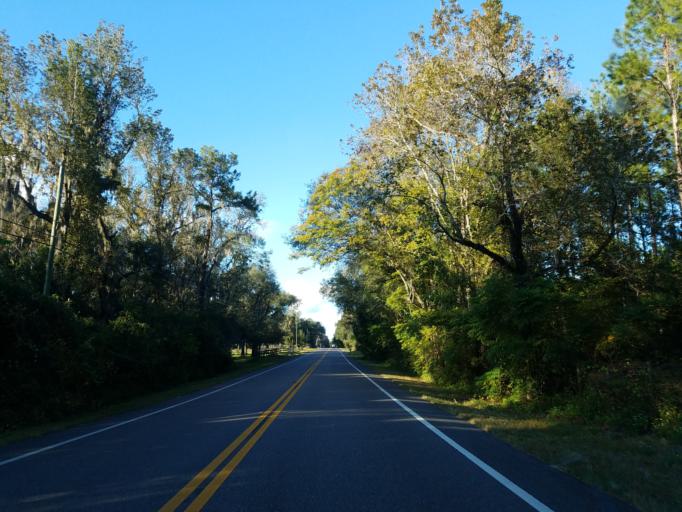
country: US
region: Florida
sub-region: Hernando County
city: Hill 'n Dale
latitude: 28.5099
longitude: -82.3031
